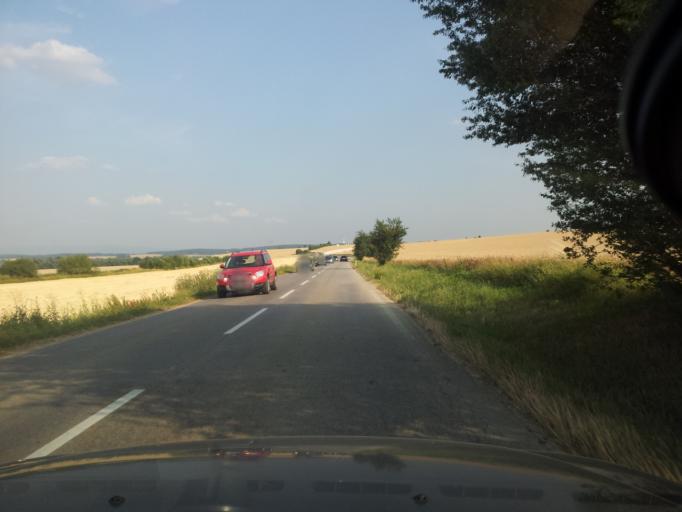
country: SK
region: Nitriansky
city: Banovce nad Bebravou
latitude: 48.7502
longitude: 18.2195
